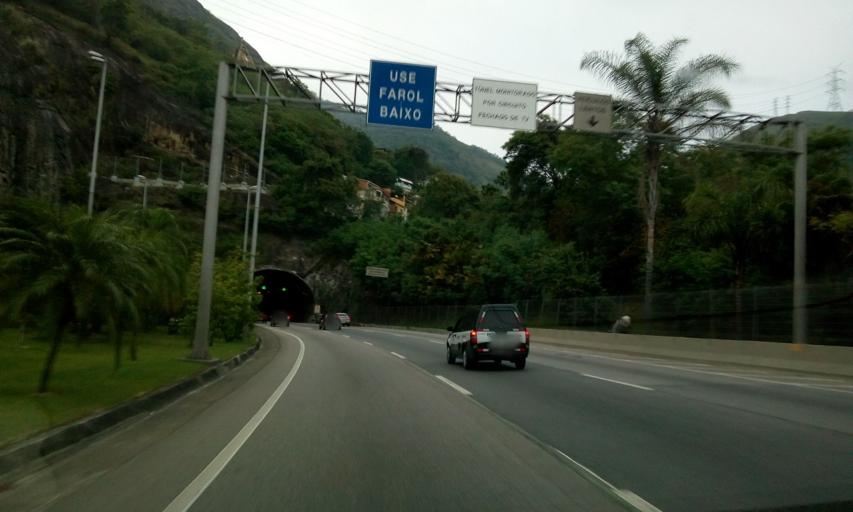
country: BR
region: Rio de Janeiro
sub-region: Rio De Janeiro
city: Rio de Janeiro
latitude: -22.9077
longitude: -43.3143
